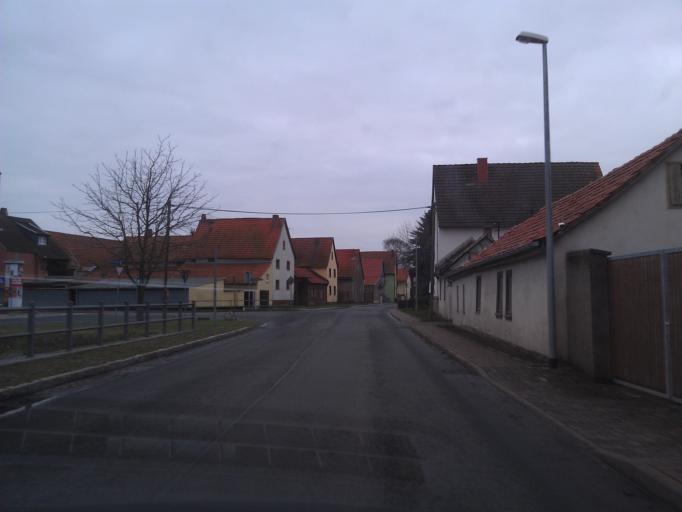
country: DE
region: Thuringia
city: Zimmernsupra
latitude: 50.9688
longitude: 10.8826
